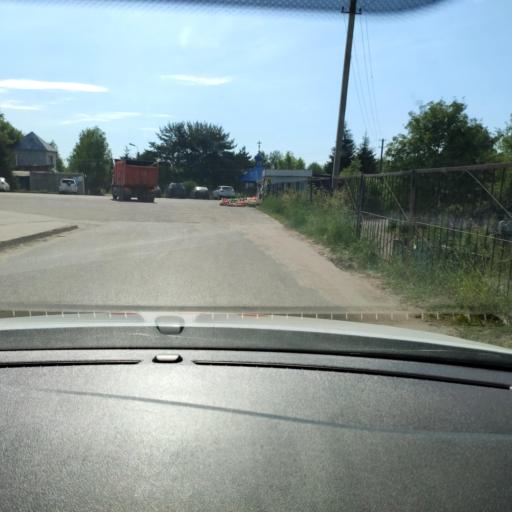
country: RU
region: Tatarstan
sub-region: Gorod Kazan'
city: Kazan
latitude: 55.8896
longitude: 49.0971
